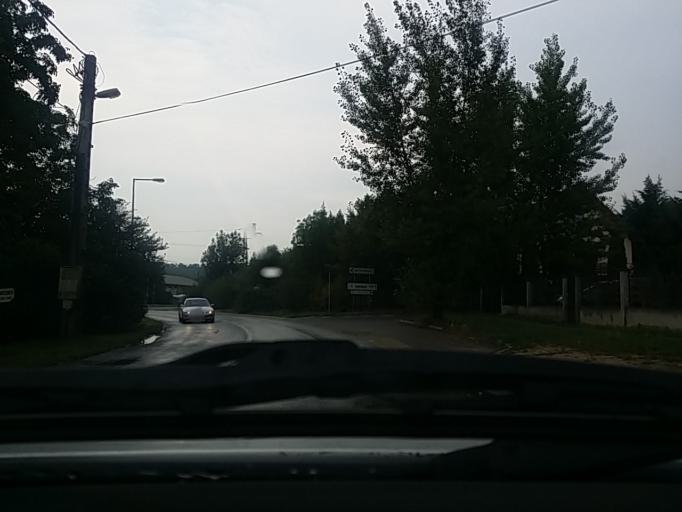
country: HU
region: Pest
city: Budakeszi
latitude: 47.5061
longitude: 18.9164
